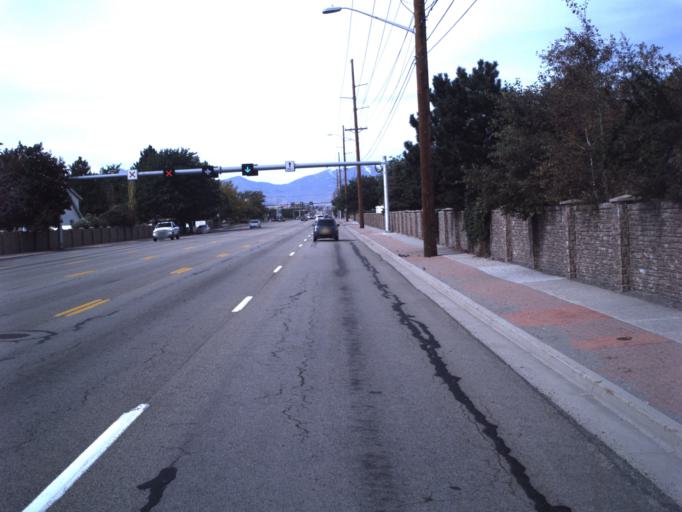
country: US
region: Utah
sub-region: Salt Lake County
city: Taylorsville
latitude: 40.6532
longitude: -111.9618
